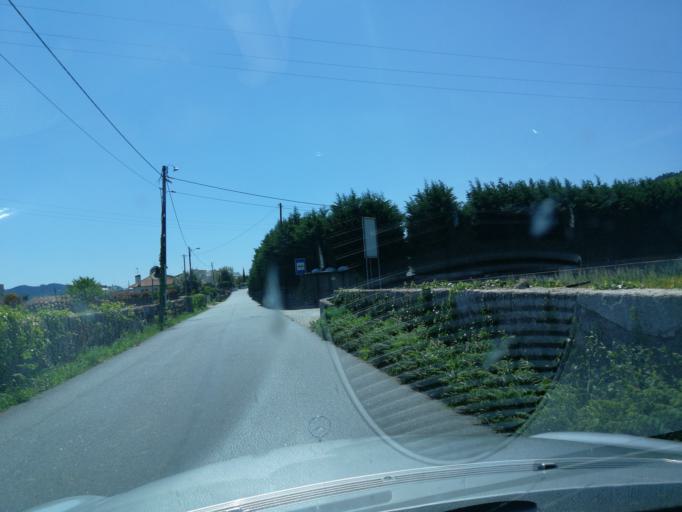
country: PT
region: Viana do Castelo
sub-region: Viana do Castelo
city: Meadela
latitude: 41.7264
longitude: -8.7898
